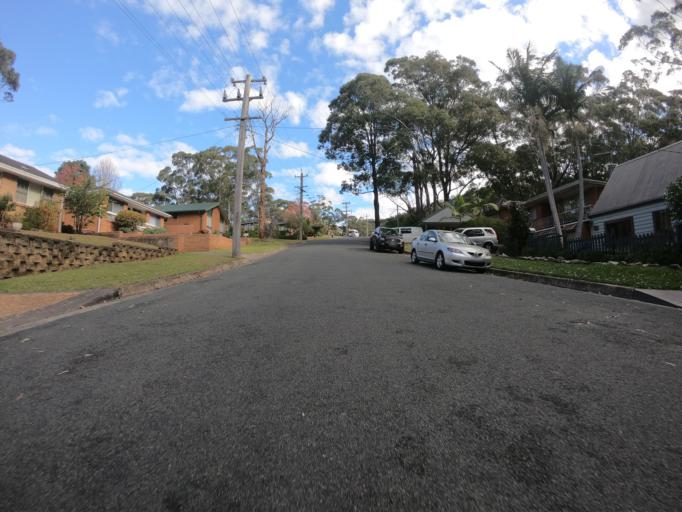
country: AU
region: New South Wales
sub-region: Wollongong
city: Bulli
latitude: -34.3323
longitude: 150.9011
